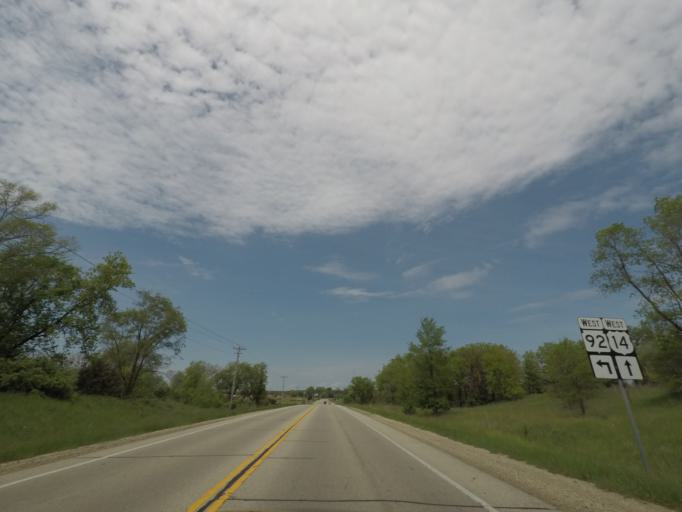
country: US
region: Wisconsin
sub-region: Green County
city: Brooklyn
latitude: 42.8521
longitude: -89.3379
